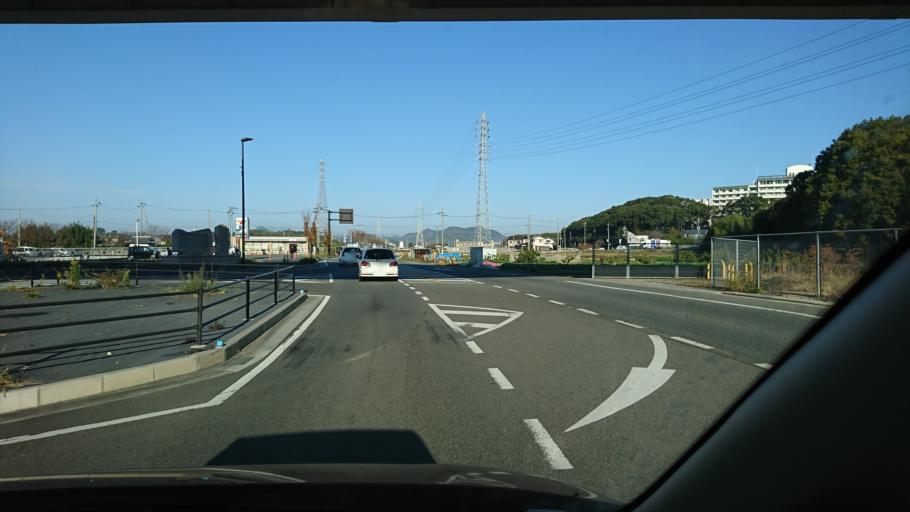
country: JP
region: Hyogo
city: Kakogawacho-honmachi
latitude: 34.7694
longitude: 134.8841
